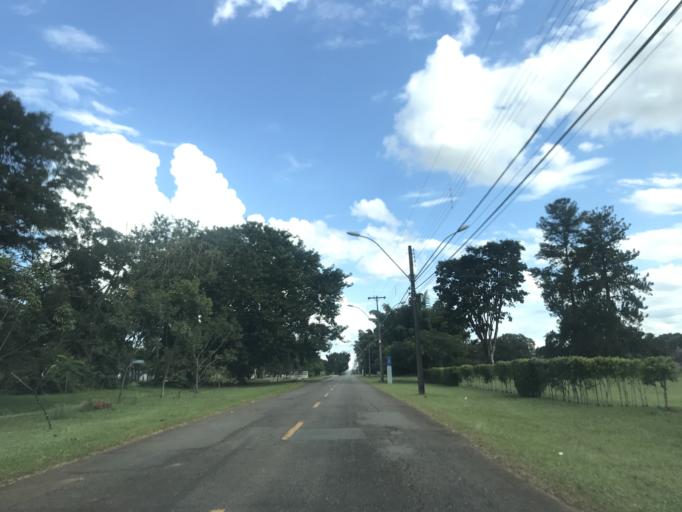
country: BR
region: Federal District
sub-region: Brasilia
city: Brasilia
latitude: -15.9040
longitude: -47.9396
